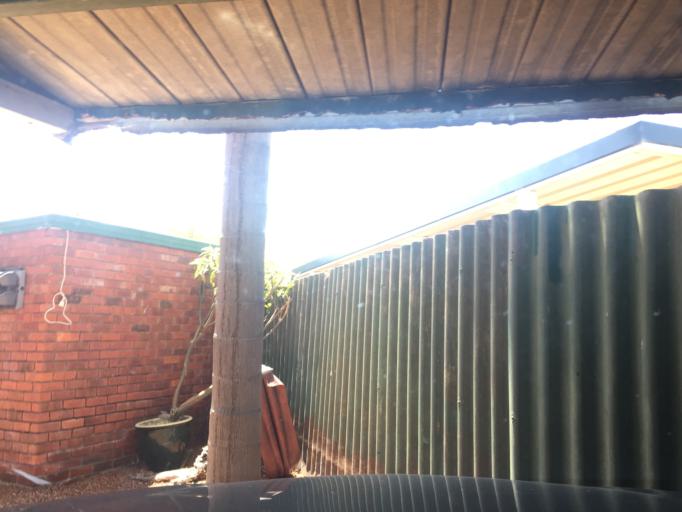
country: AU
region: Western Australia
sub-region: Canning
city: Ferndale
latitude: -32.0435
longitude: 115.9117
